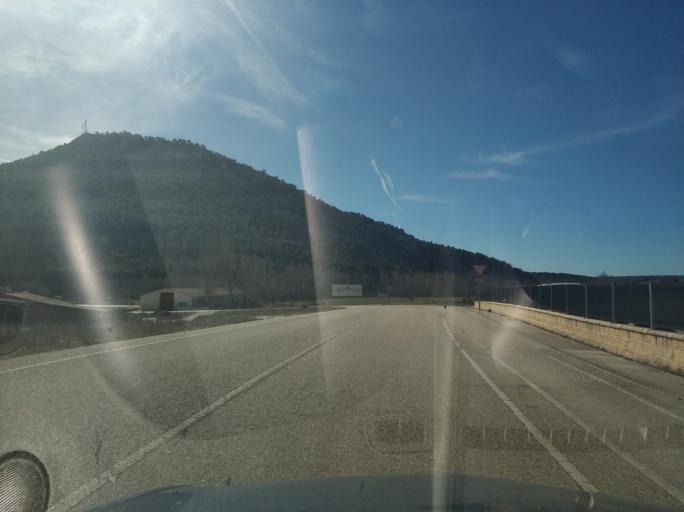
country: ES
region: Castille and Leon
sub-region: Provincia de Soria
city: San Leonardo de Yague
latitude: 41.8256
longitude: -3.0820
